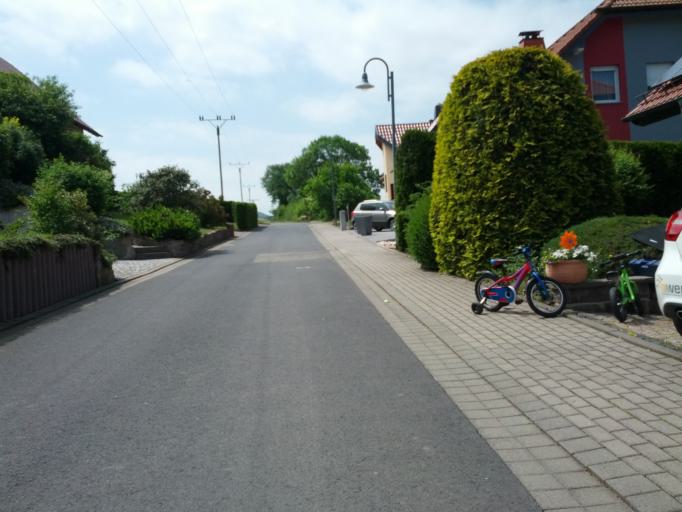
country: DE
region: Thuringia
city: Urnshausen
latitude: 50.7299
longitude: 10.1731
